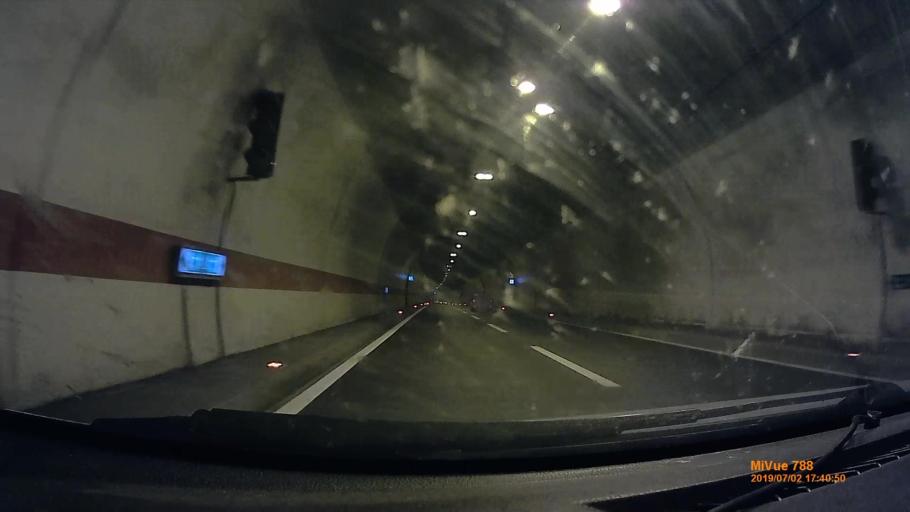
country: HR
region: Primorsko-Goranska
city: Vrbovsko
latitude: 45.3806
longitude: 14.9479
